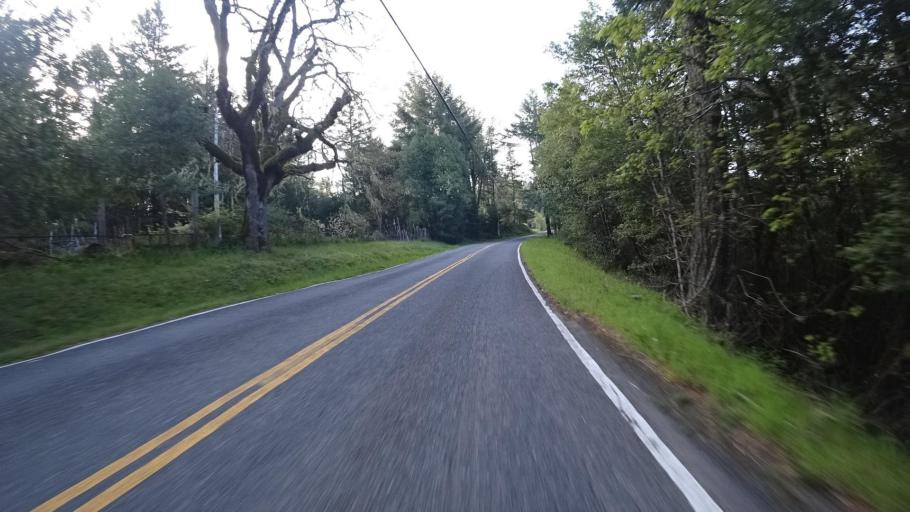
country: US
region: California
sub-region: Humboldt County
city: Blue Lake
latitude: 40.7422
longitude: -123.9605
